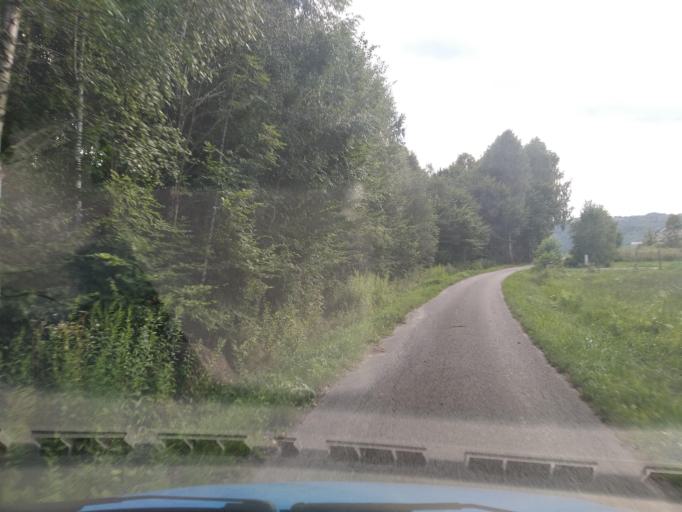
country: PL
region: Subcarpathian Voivodeship
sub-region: Powiat strzyzowski
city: Polomia
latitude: 49.8934
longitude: 21.9078
